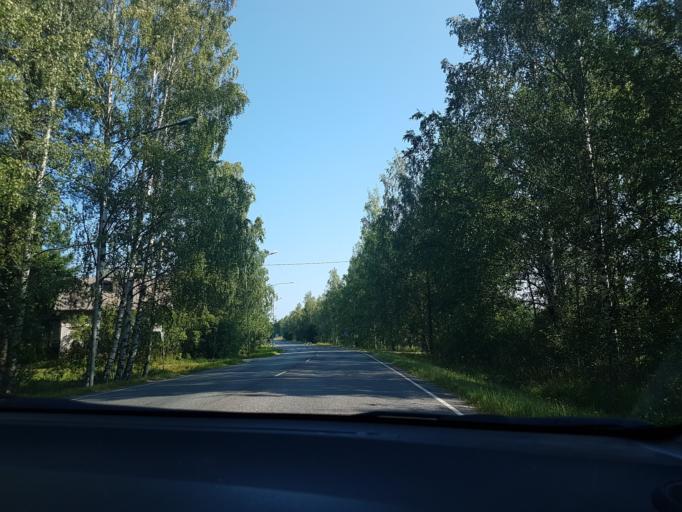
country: FI
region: Uusimaa
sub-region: Helsinki
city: Kerava
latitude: 60.3892
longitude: 25.0998
